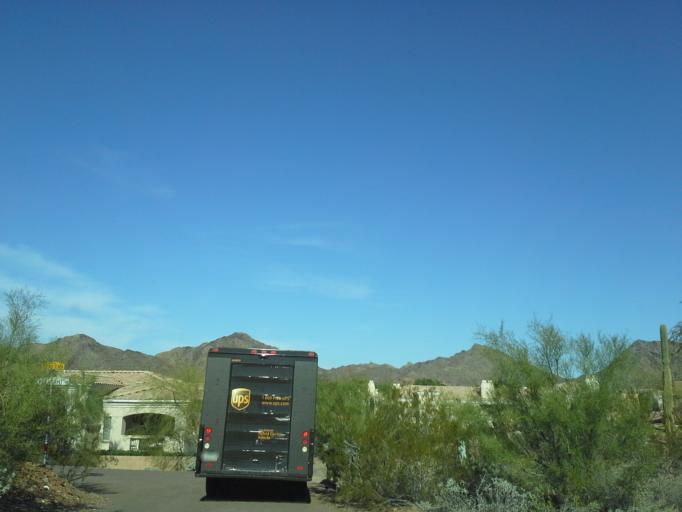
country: US
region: Arizona
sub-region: Maricopa County
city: Paradise Valley
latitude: 33.5531
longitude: -112.0437
